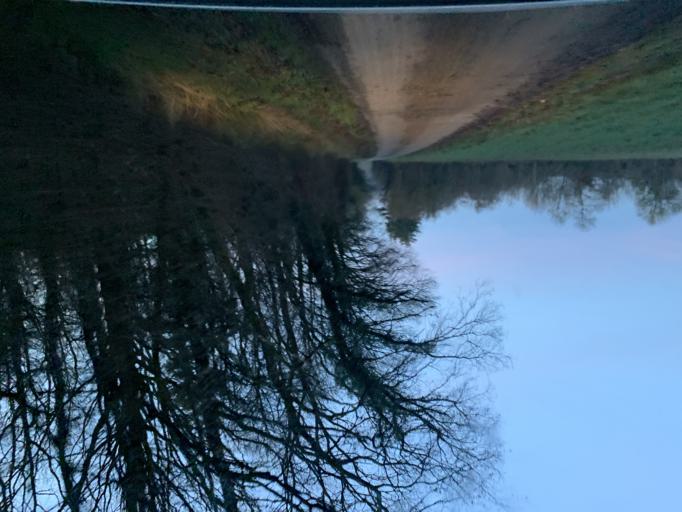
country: FR
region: Bourgogne
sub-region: Departement de l'Yonne
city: Fontenailles
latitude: 47.5571
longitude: 3.3592
